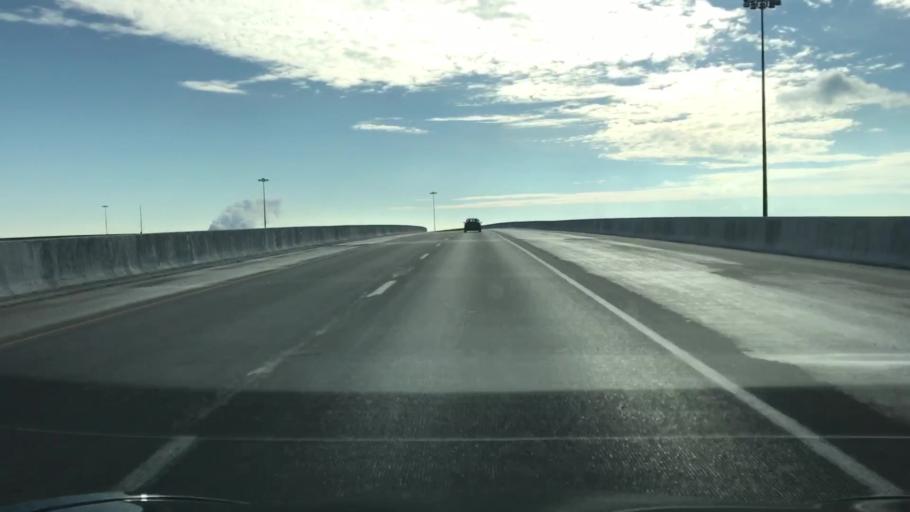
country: US
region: Nebraska
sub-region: Douglas County
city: Omaha
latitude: 41.2354
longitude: -95.8998
